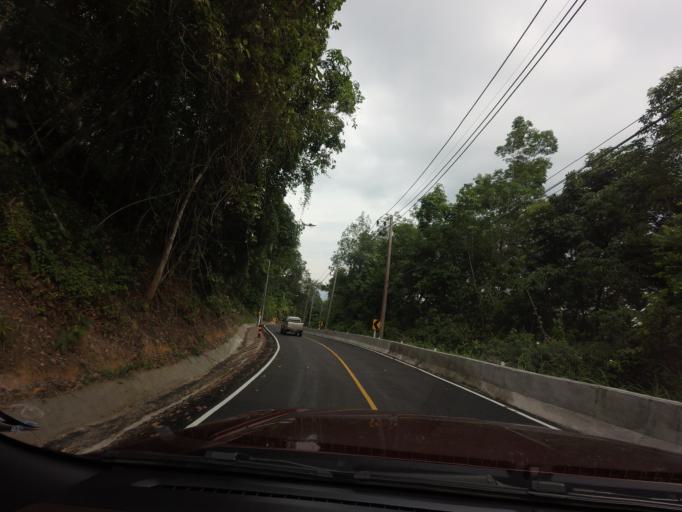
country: TH
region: Yala
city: Than To
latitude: 6.1357
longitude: 101.2963
